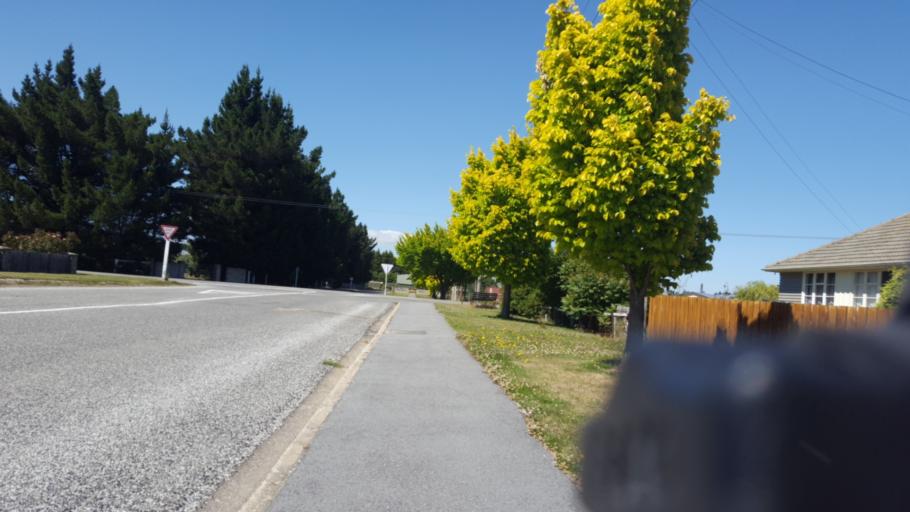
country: NZ
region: Otago
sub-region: Dunedin City
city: Dunedin
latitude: -45.1299
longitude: 170.1060
